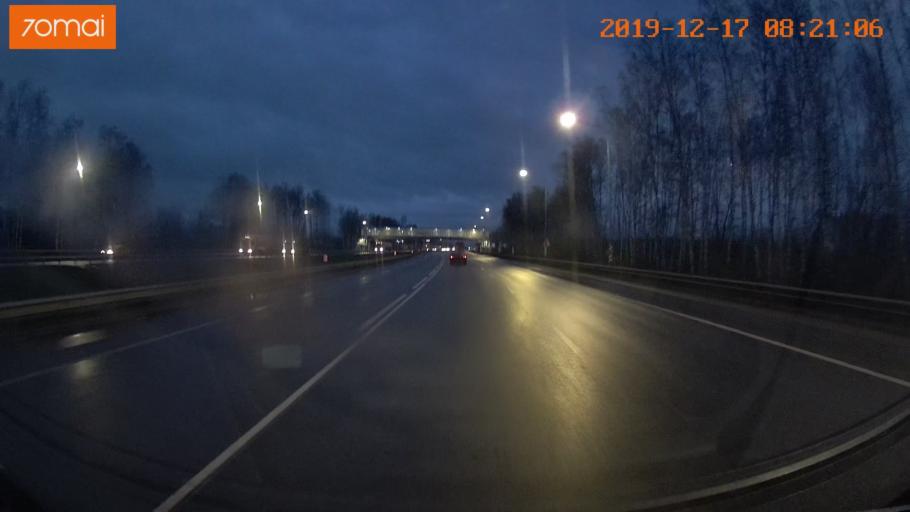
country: RU
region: Vladimir
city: Vorsha
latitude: 56.0754
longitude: 40.1775
